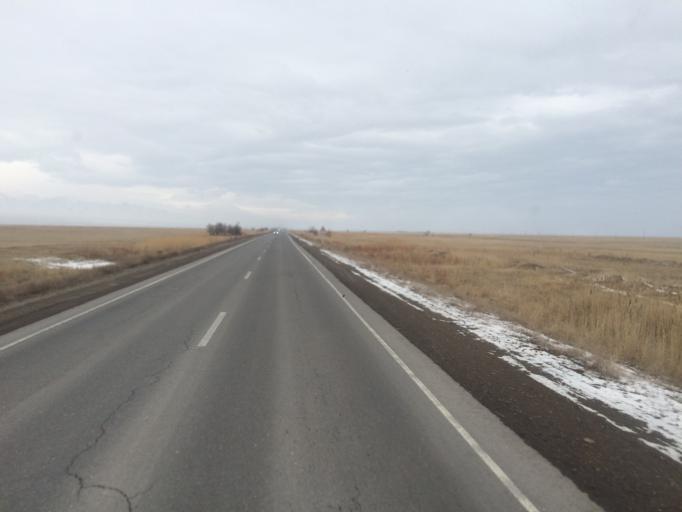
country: KG
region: Chuy
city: Tokmok
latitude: 43.3534
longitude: 75.4489
